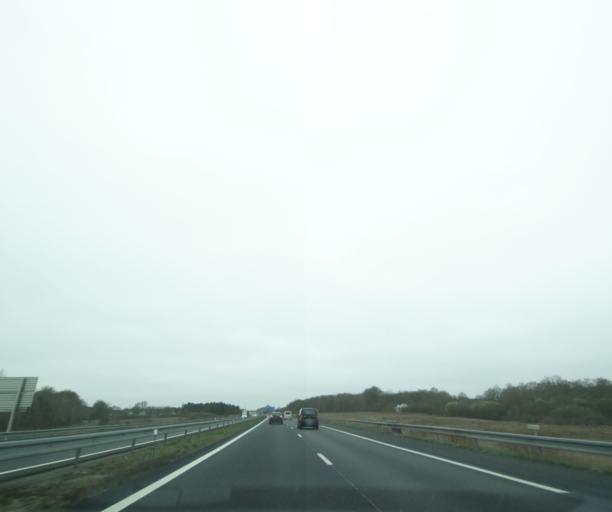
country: FR
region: Centre
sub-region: Departement du Loir-et-Cher
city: Theillay
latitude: 47.2971
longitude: 2.0448
